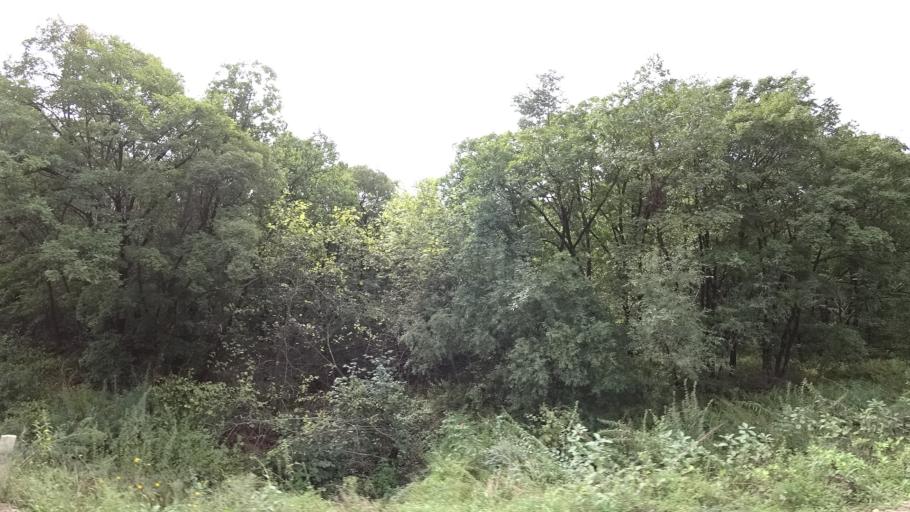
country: RU
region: Primorskiy
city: Lyalichi
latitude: 44.0979
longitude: 132.4292
